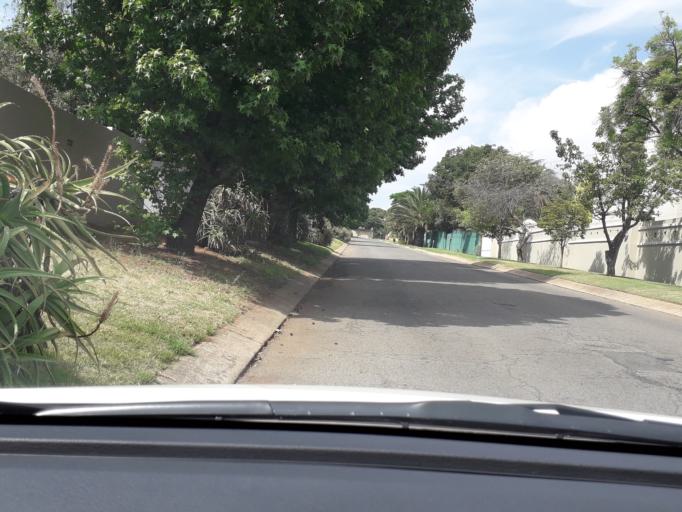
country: ZA
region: Gauteng
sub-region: City of Johannesburg Metropolitan Municipality
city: Modderfontein
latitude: -26.1029
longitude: 28.0659
